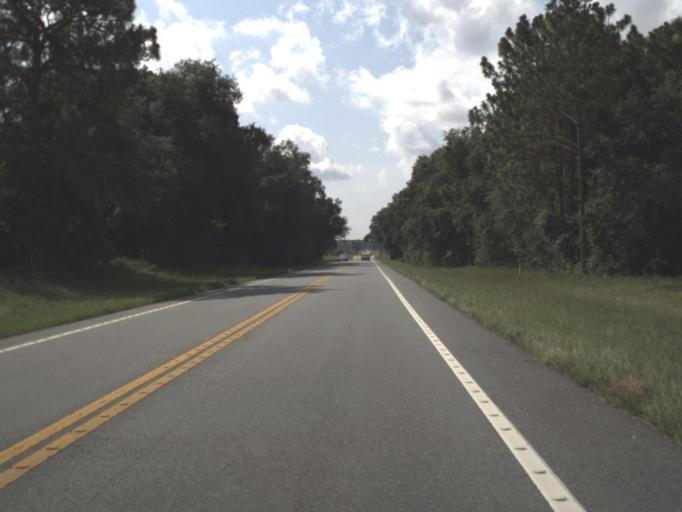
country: US
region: Florida
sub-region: Citrus County
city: Citrus Springs
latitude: 28.9838
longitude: -82.4329
